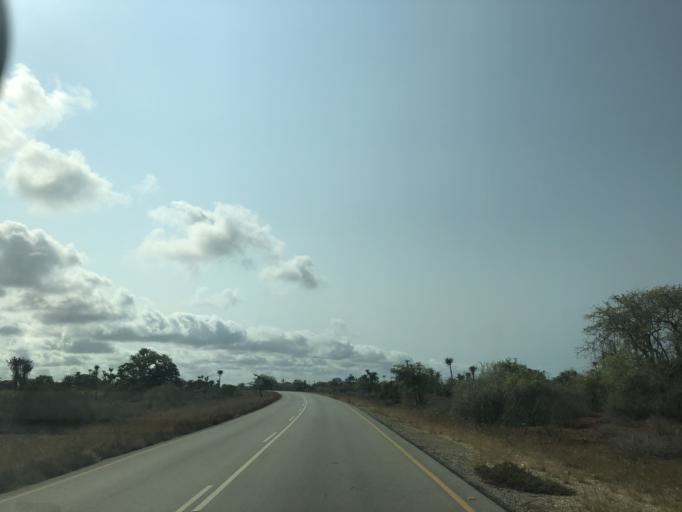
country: AO
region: Luanda
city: Luanda
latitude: -9.7066
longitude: 13.2175
